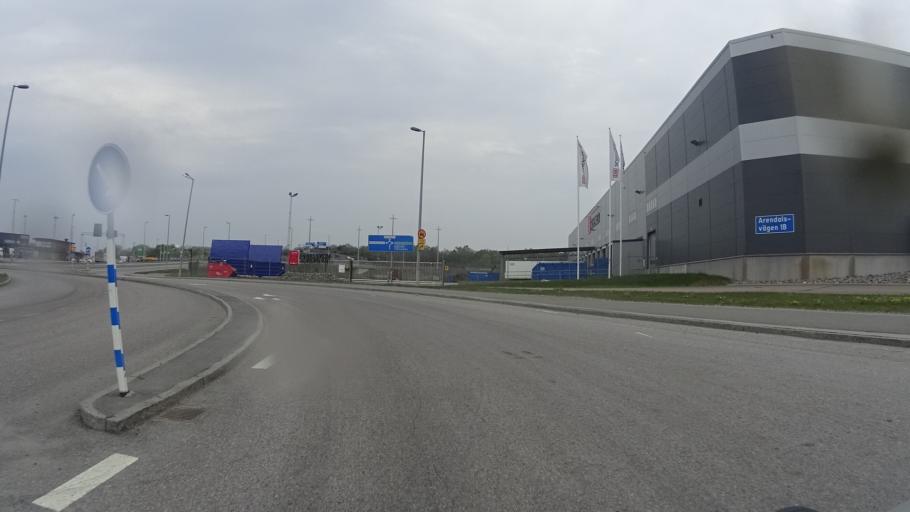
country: SE
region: Vaestra Goetaland
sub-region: Goteborg
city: Majorna
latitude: 57.7012
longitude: 11.8615
